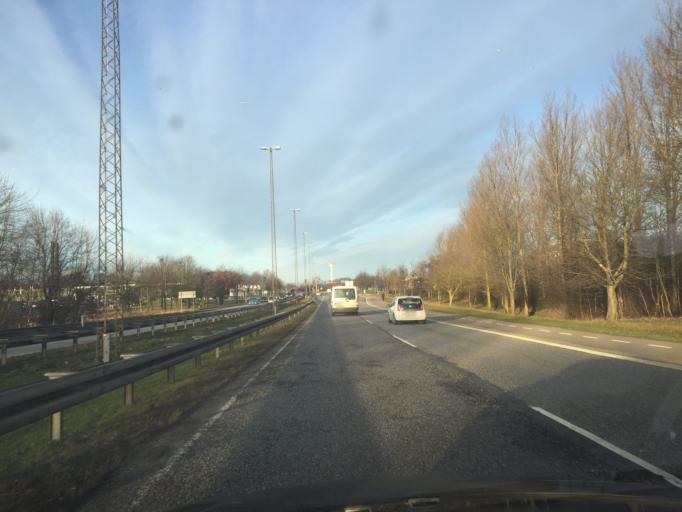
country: DK
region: Capital Region
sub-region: Hoje-Taastrup Kommune
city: Taastrup
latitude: 55.6526
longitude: 12.2825
